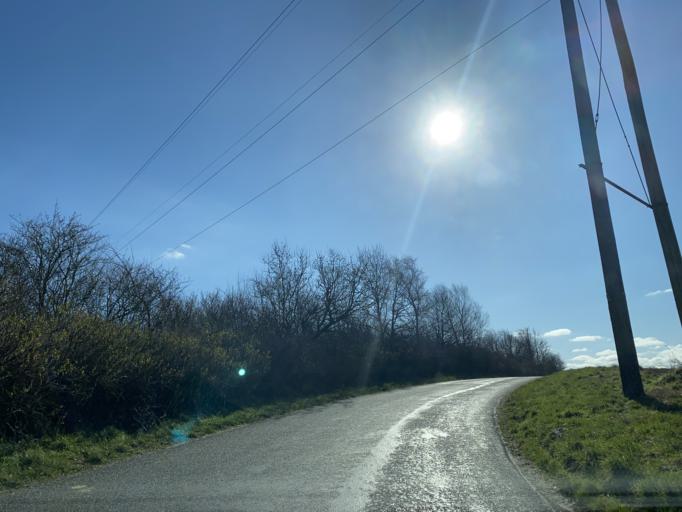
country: DK
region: Central Jutland
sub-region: Arhus Kommune
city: Framlev
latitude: 56.1773
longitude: 10.0432
